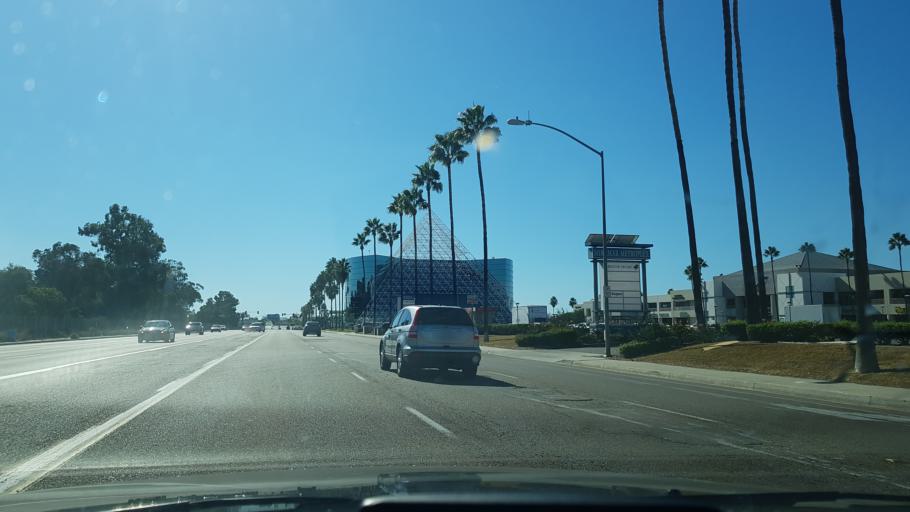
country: US
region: California
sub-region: San Diego County
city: Fairbanks Ranch
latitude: 32.8838
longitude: -117.1532
